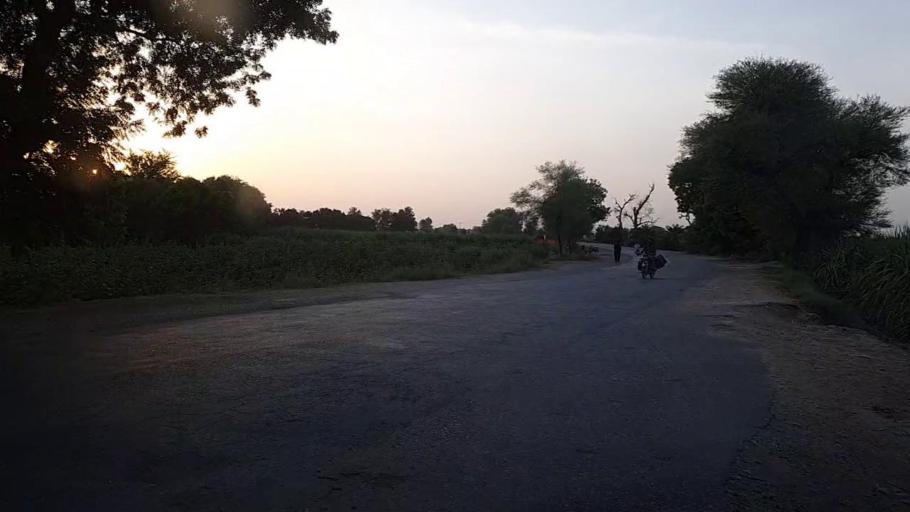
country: PK
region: Sindh
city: Ubauro
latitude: 28.3030
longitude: 69.7938
